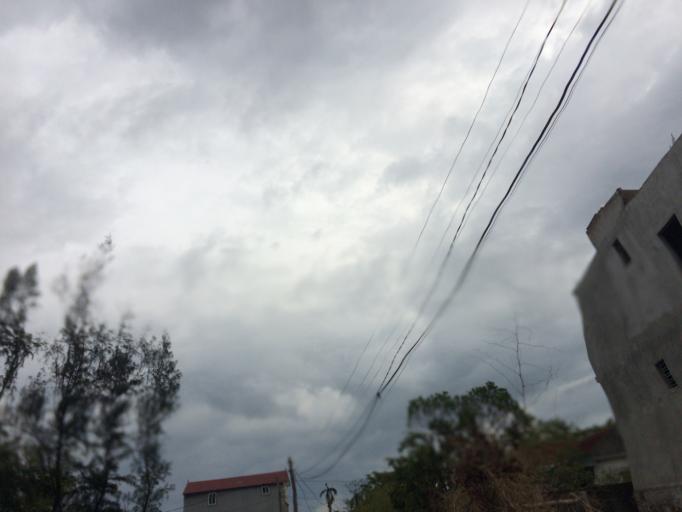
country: VN
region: Ha Tinh
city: Ha Tinh
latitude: 18.3622
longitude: 105.8910
